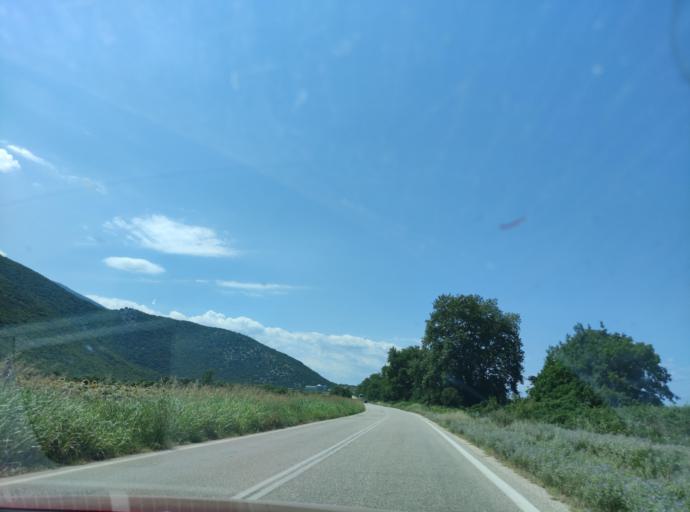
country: GR
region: East Macedonia and Thrace
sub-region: Nomos Kavalas
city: Palaiochori
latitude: 40.9670
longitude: 24.1791
